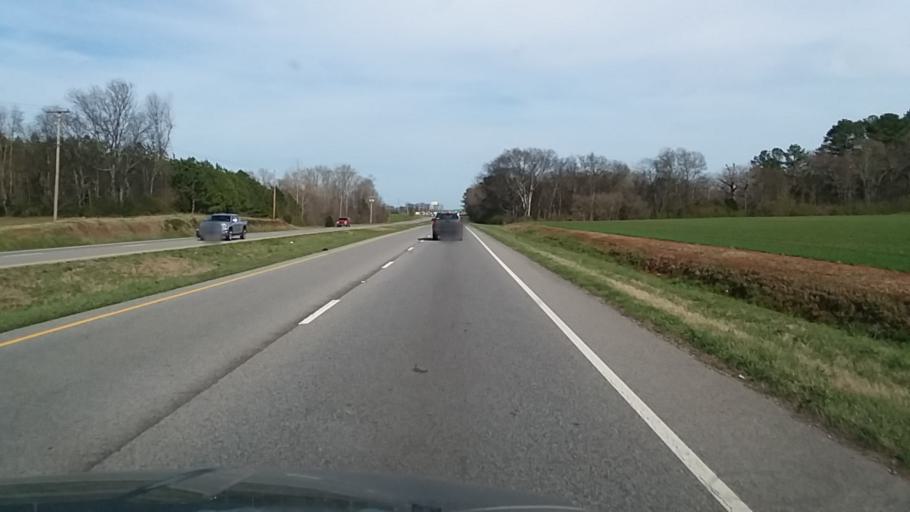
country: US
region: Alabama
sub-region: Morgan County
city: Decatur
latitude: 34.6283
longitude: -86.9279
